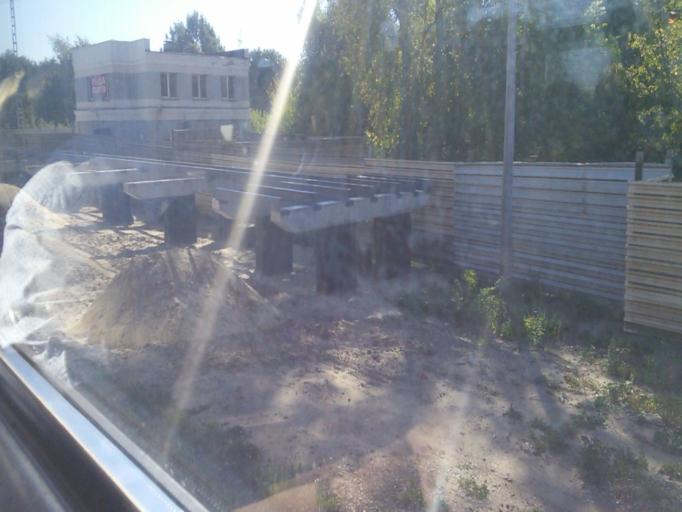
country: RU
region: Moscow
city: Perovo
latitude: 55.7389
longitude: 37.7916
